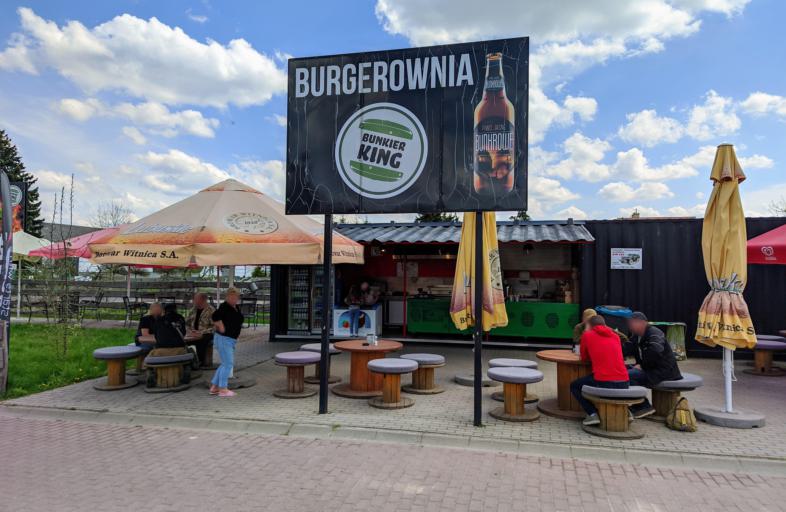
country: PL
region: Lubusz
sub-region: Powiat swiebodzinski
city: Lubrza
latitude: 52.3718
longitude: 15.5072
